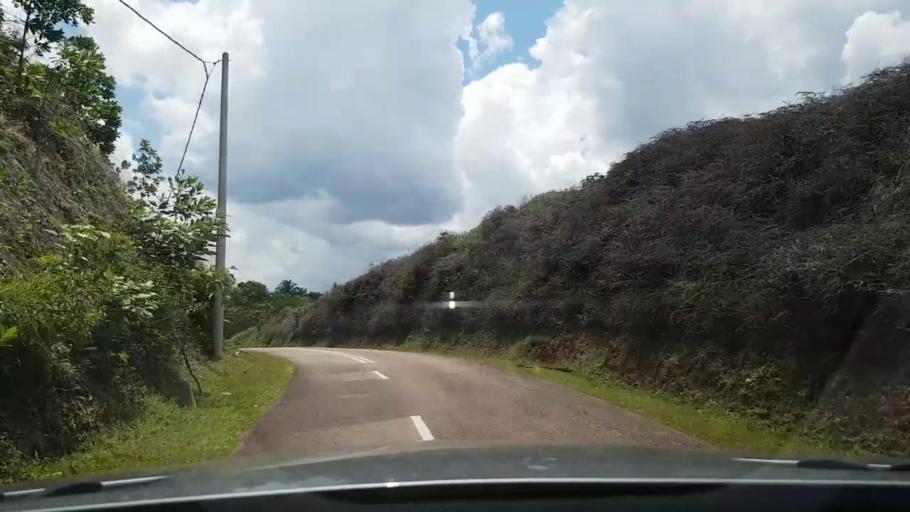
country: MY
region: Pahang
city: Pekan
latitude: 3.0982
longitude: 102.9786
